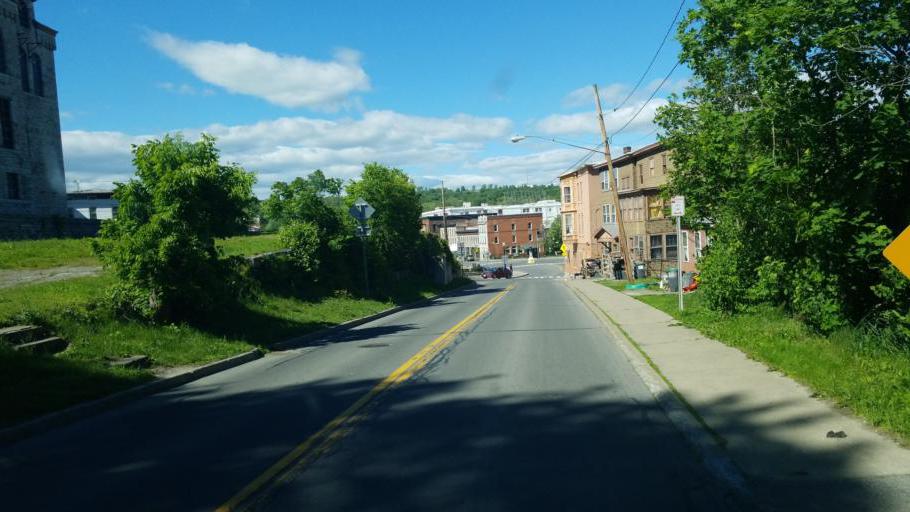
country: US
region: New York
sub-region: Montgomery County
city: Canajoharie
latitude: 42.9042
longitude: -74.5732
